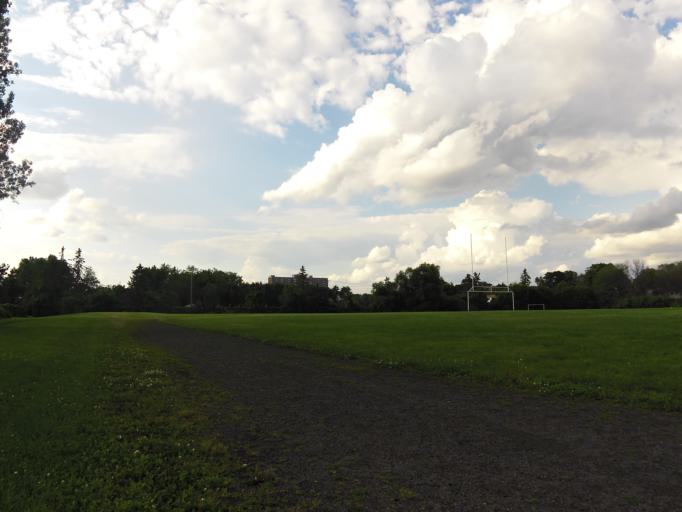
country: CA
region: Ontario
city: Bells Corners
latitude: 45.3432
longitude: -75.7944
